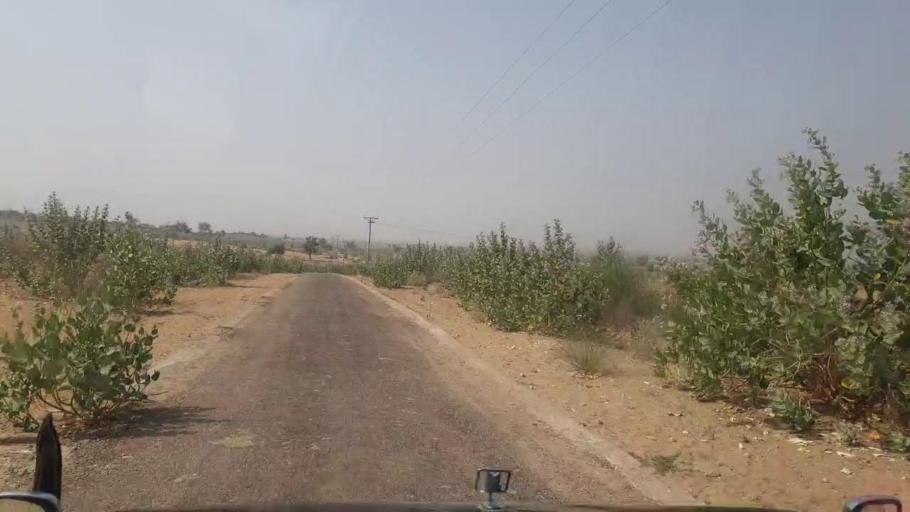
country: PK
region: Sindh
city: Islamkot
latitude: 25.0982
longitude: 70.1803
